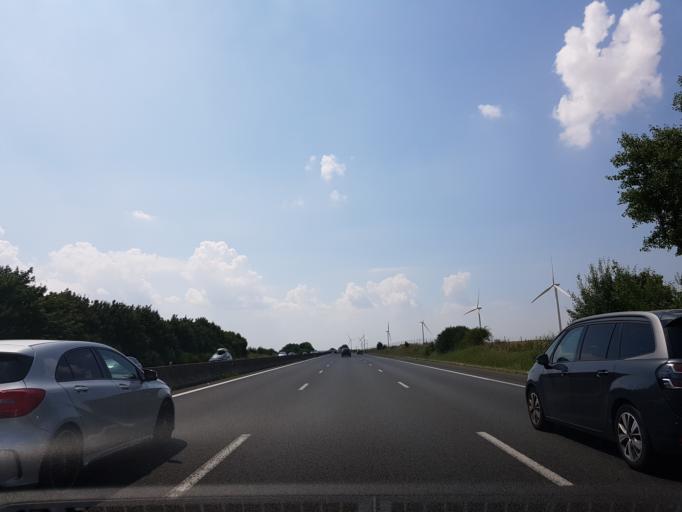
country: FR
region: Centre
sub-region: Departement d'Eure-et-Loir
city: Aunay-sous-Auneau
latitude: 48.3327
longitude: 1.8655
